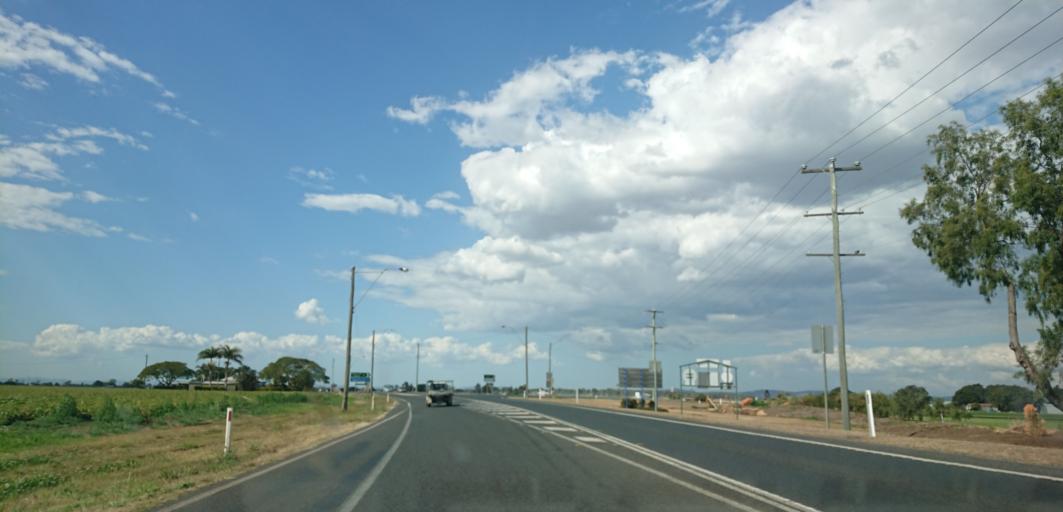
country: AU
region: Queensland
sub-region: Lockyer Valley
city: Gatton
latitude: -27.5548
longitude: 152.3041
